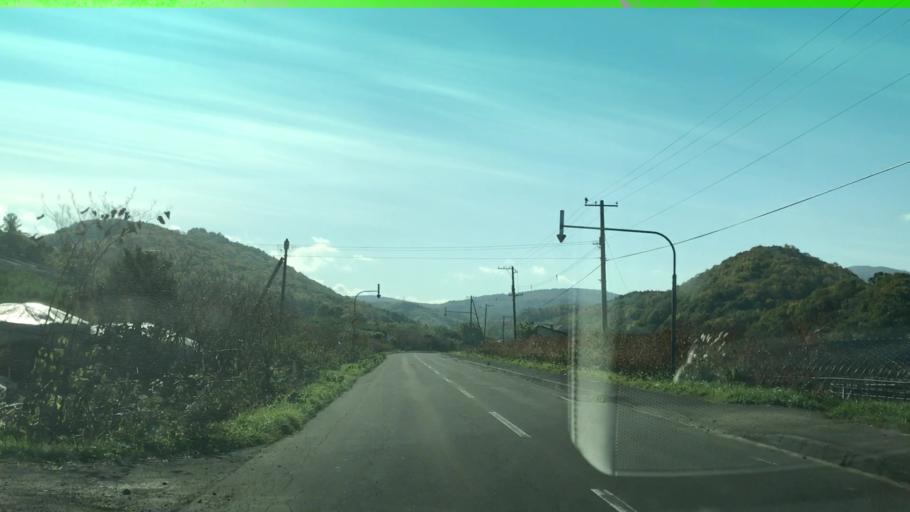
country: JP
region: Hokkaido
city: Yoichi
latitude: 43.1583
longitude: 140.8221
